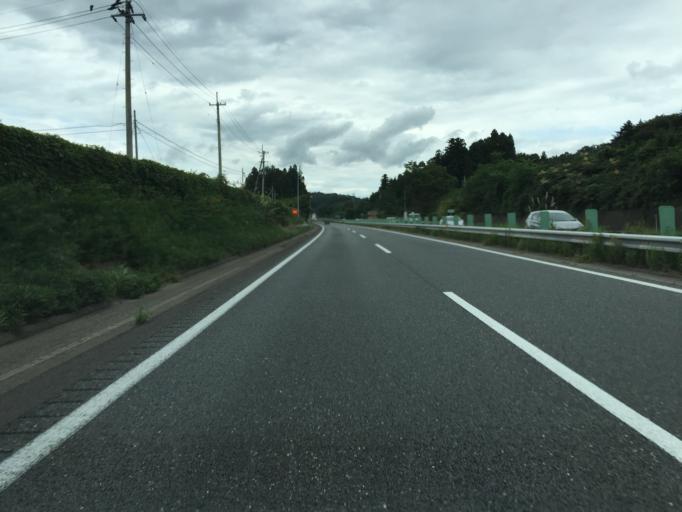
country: JP
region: Miyagi
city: Okawara
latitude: 38.1105
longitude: 140.6955
